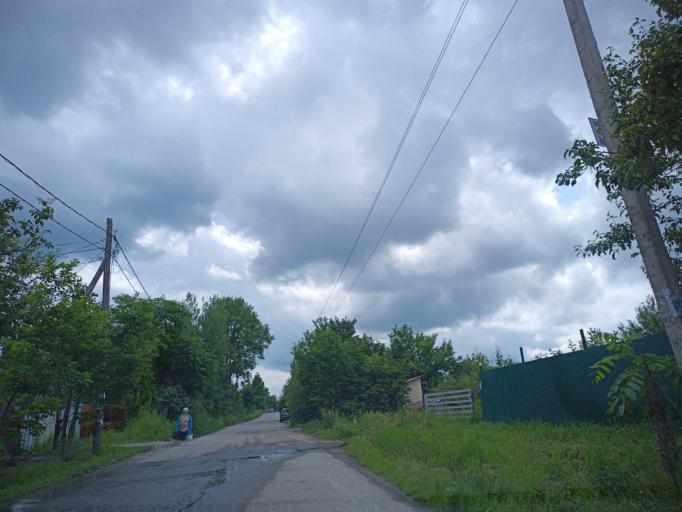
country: RU
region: Khabarovsk Krai
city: Korfovskiy
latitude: 48.3129
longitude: 135.1016
